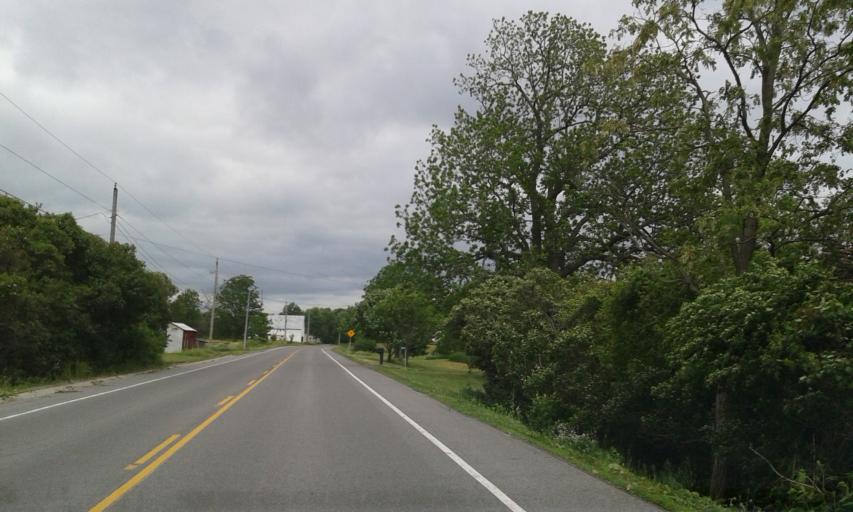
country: CA
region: Ontario
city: Napanee Downtown
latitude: 44.1073
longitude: -76.9264
